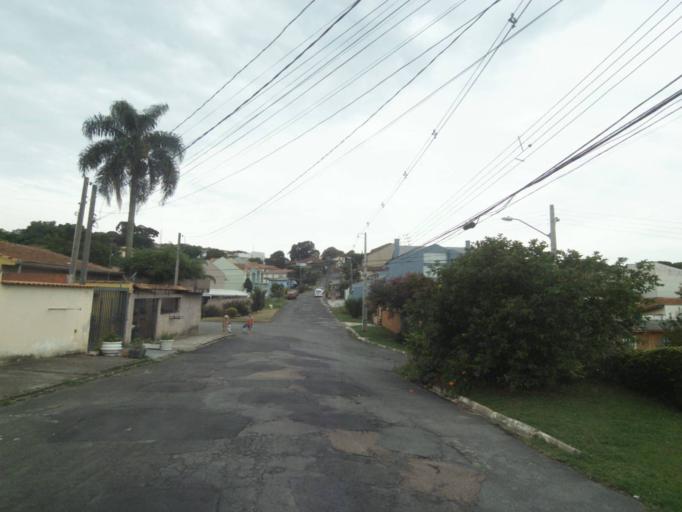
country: BR
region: Parana
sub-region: Curitiba
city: Curitiba
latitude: -25.4126
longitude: -49.3000
